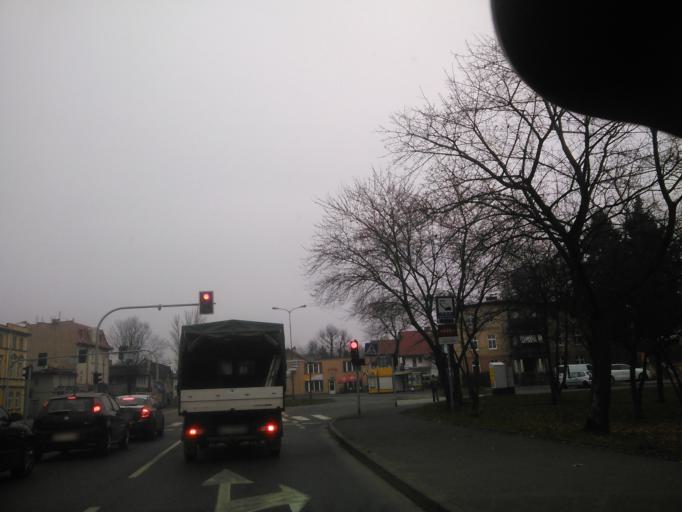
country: PL
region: Lower Silesian Voivodeship
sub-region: Jelenia Gora
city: Cieplice Slaskie Zdroj
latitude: 50.8631
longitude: 15.6880
